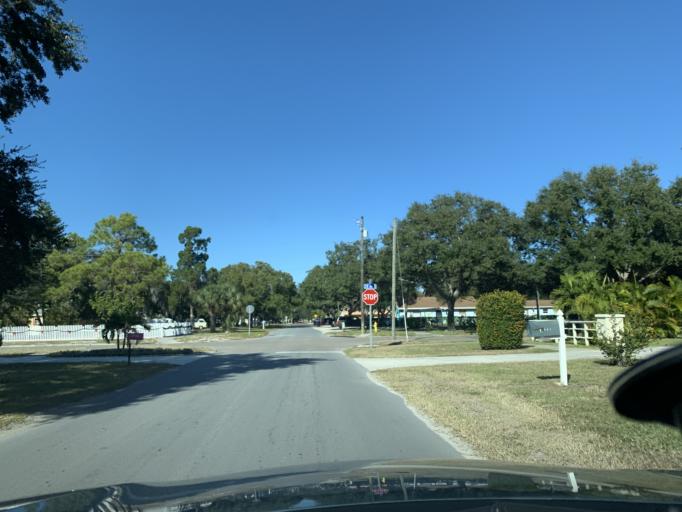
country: US
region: Florida
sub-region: Pinellas County
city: Gulfport
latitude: 27.7419
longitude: -82.7065
